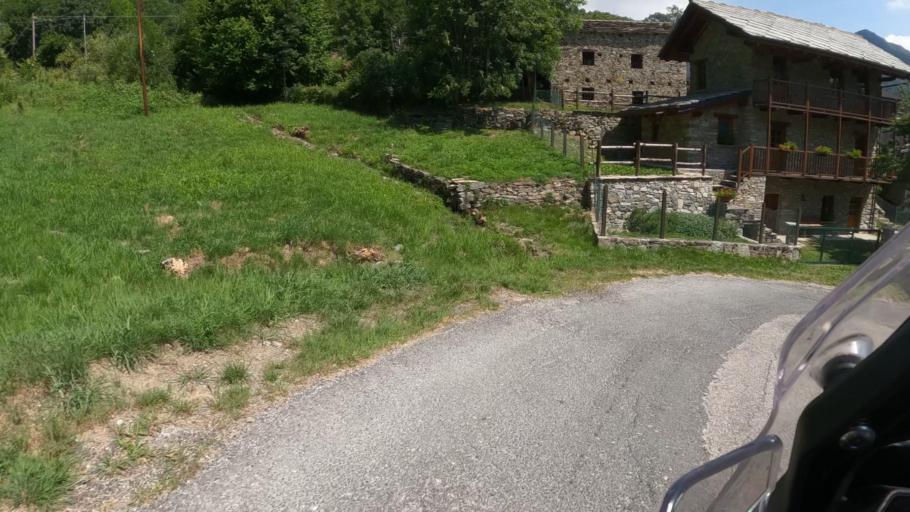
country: IT
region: Piedmont
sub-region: Provincia di Torino
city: Sant'Antonino di Susa
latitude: 45.1432
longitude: 7.2761
